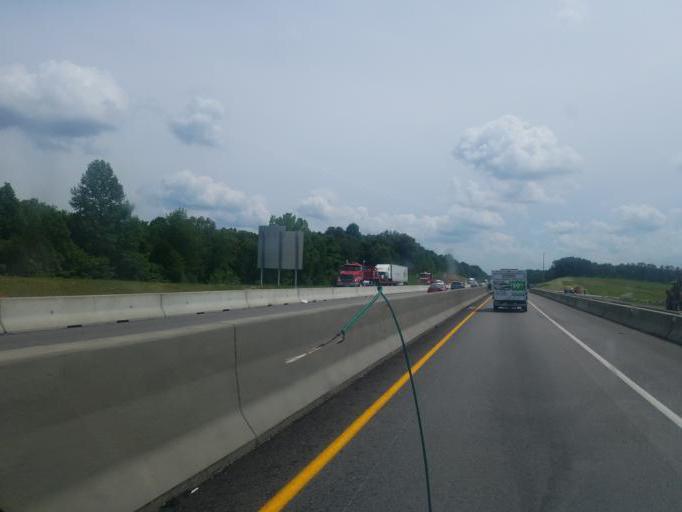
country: US
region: Kentucky
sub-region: Hardin County
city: Elizabethtown
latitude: 37.6515
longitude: -85.8565
